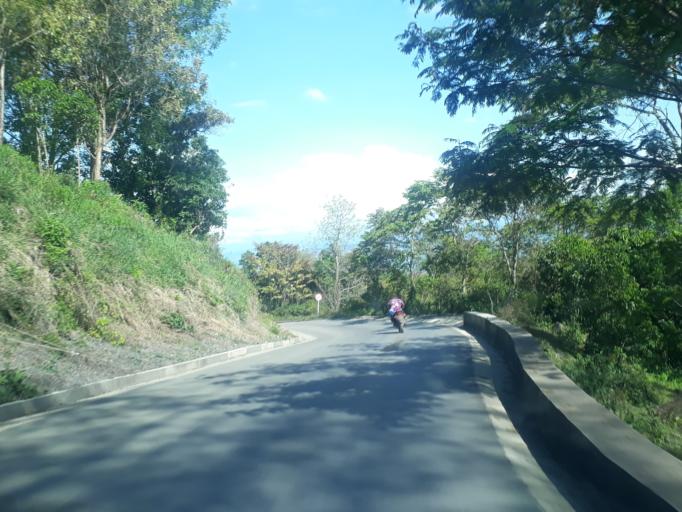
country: CO
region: Santander
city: Velez
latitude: 6.0244
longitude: -73.6577
